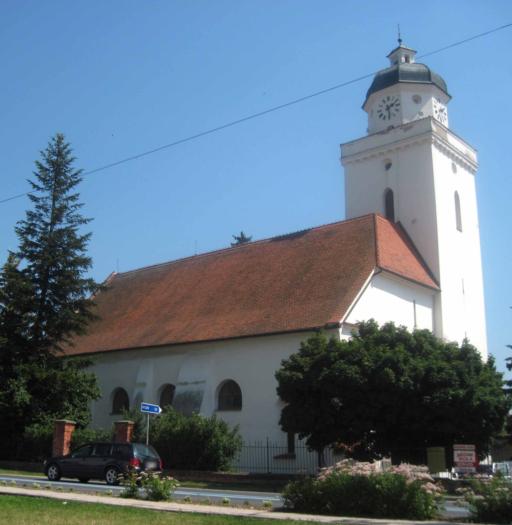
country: CZ
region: South Moravian
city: Pohorelice
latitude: 48.9811
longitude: 16.5230
